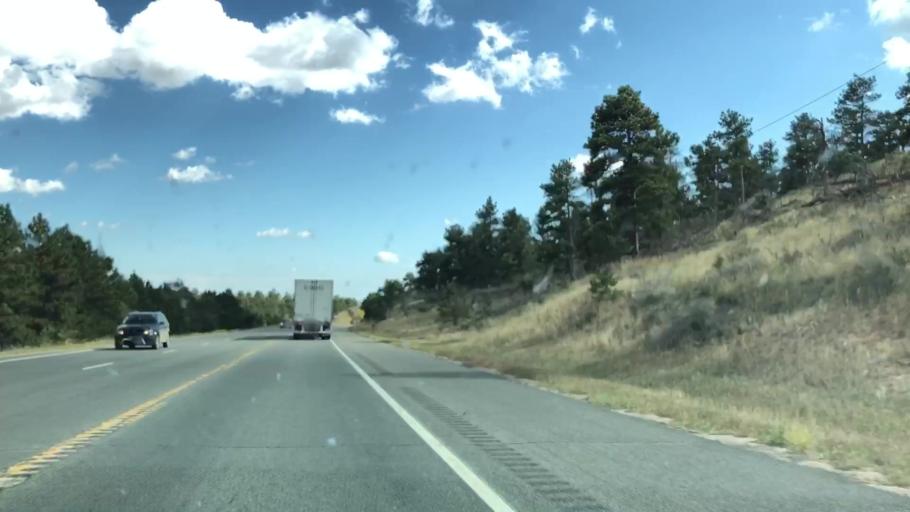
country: US
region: Wyoming
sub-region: Albany County
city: Laramie
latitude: 40.9770
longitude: -105.3870
